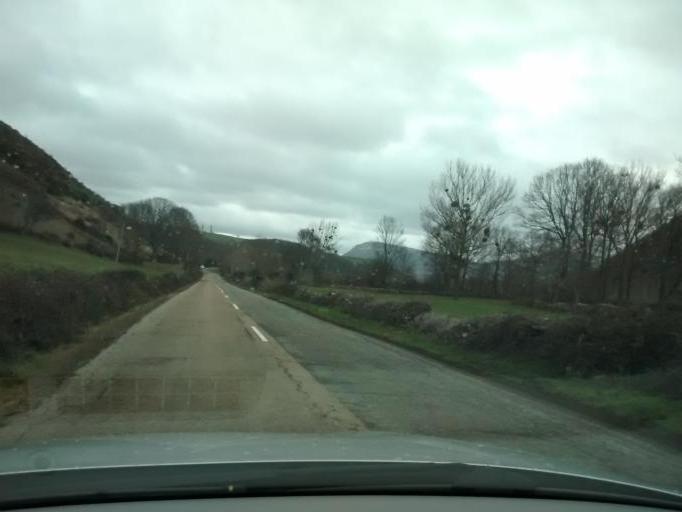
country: ES
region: Castille and Leon
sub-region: Provincia de Burgos
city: Espinosa de los Monteros
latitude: 43.0925
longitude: -3.5609
